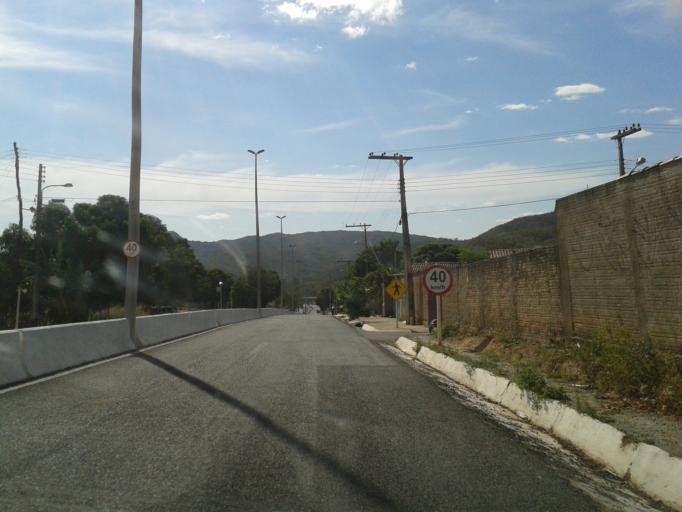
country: BR
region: Goias
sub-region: Goias
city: Goias
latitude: -15.9462
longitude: -50.1313
